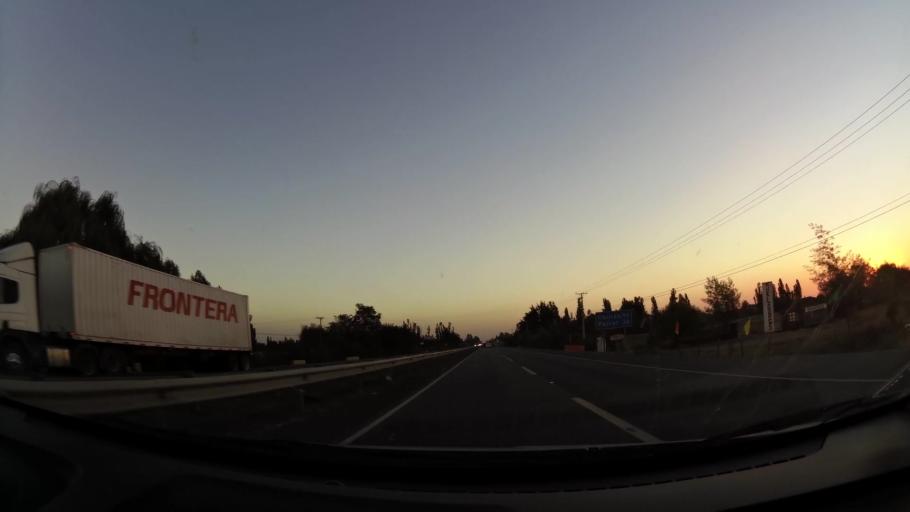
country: CL
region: Maule
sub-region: Provincia de Linares
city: Linares
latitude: -35.8935
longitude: -71.6456
